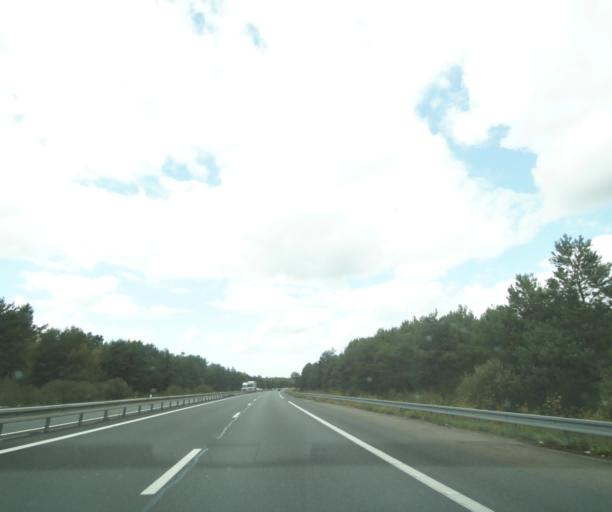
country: FR
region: Centre
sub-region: Departement du Loiret
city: La Ferte-Saint-Aubin
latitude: 47.6829
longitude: 1.9059
